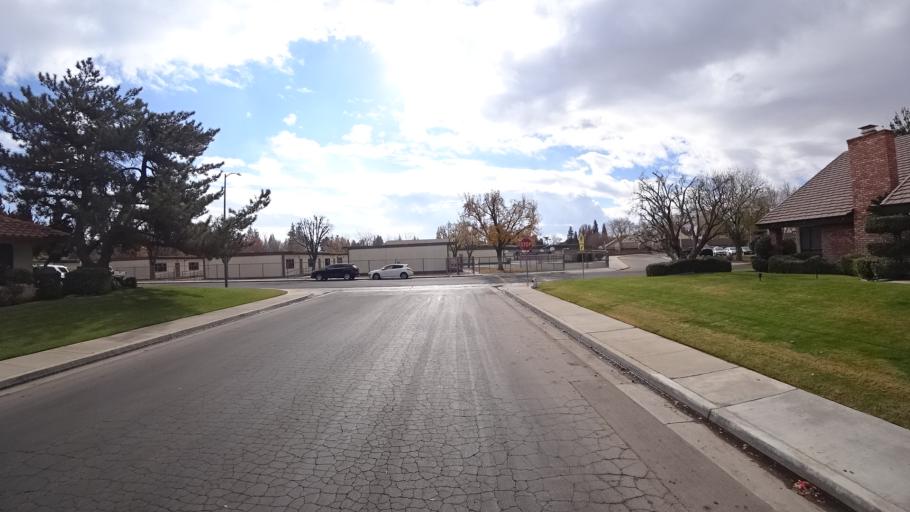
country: US
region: California
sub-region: Kern County
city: Greenacres
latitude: 35.3504
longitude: -119.0886
